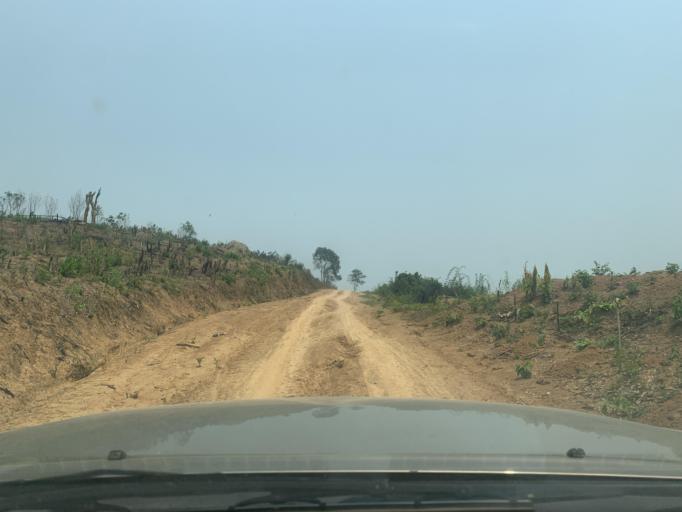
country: LA
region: Louangphabang
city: Xiang Ngeun
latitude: 19.8349
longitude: 102.2251
